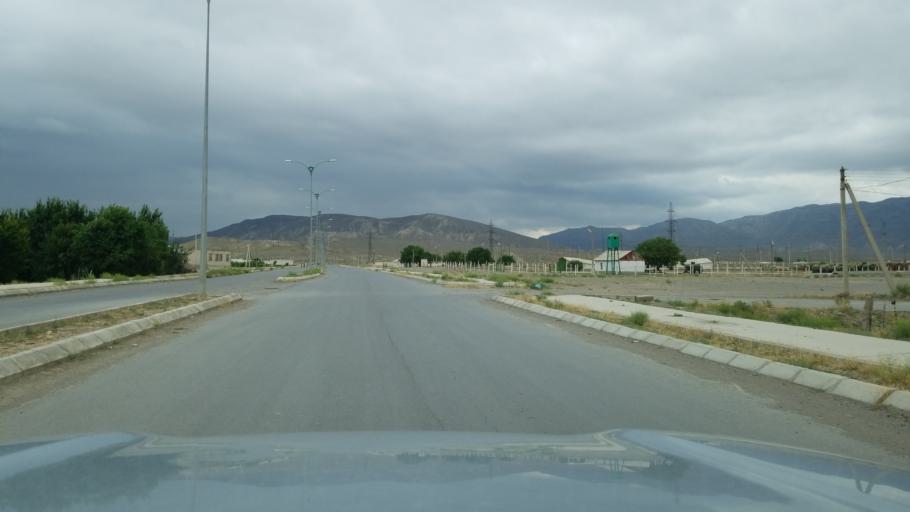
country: TM
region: Balkan
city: Serdar
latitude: 38.9680
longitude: 56.2634
